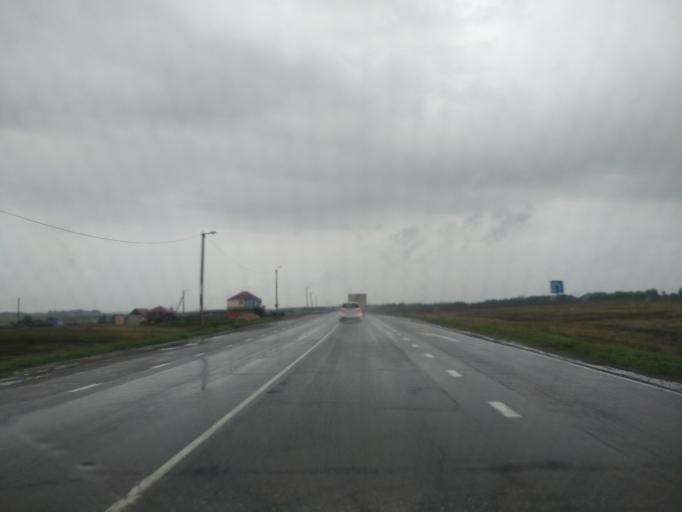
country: RU
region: Voronezj
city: Verkhnyaya Khava
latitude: 51.6782
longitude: 39.8793
